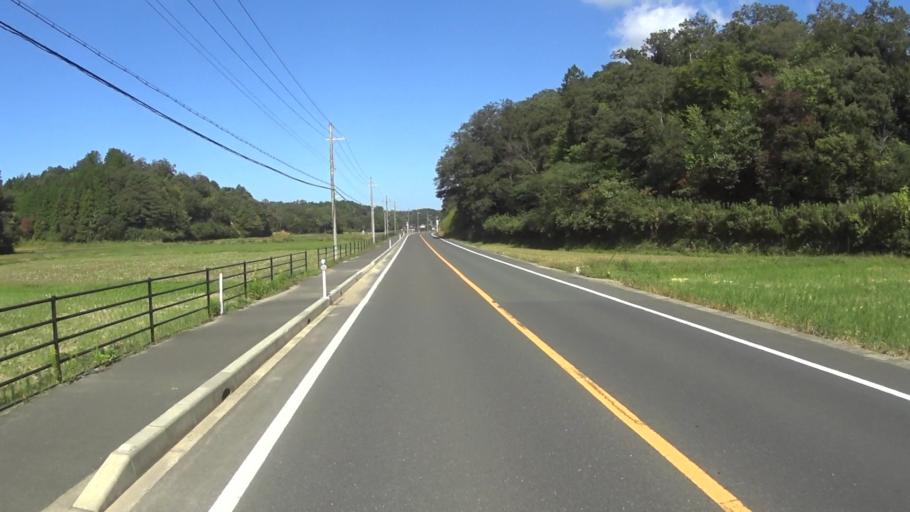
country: JP
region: Kyoto
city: Miyazu
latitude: 35.6469
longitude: 135.0697
